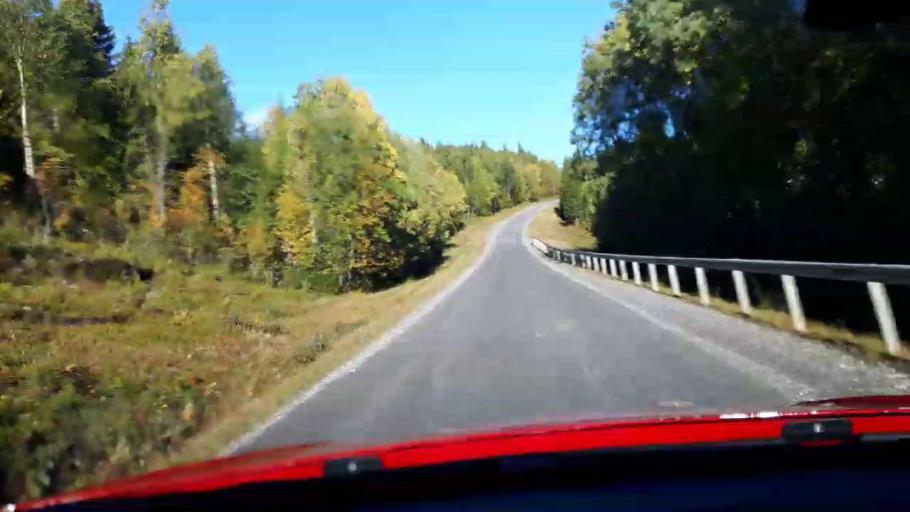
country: NO
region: Nord-Trondelag
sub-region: Lierne
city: Sandvika
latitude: 64.5786
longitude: 13.8941
